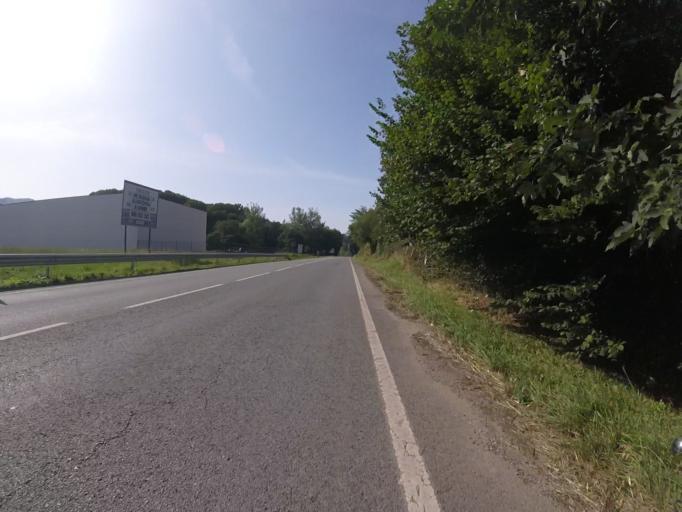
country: ES
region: Navarre
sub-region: Provincia de Navarra
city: Zugarramurdi
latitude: 43.1785
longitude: -1.4916
